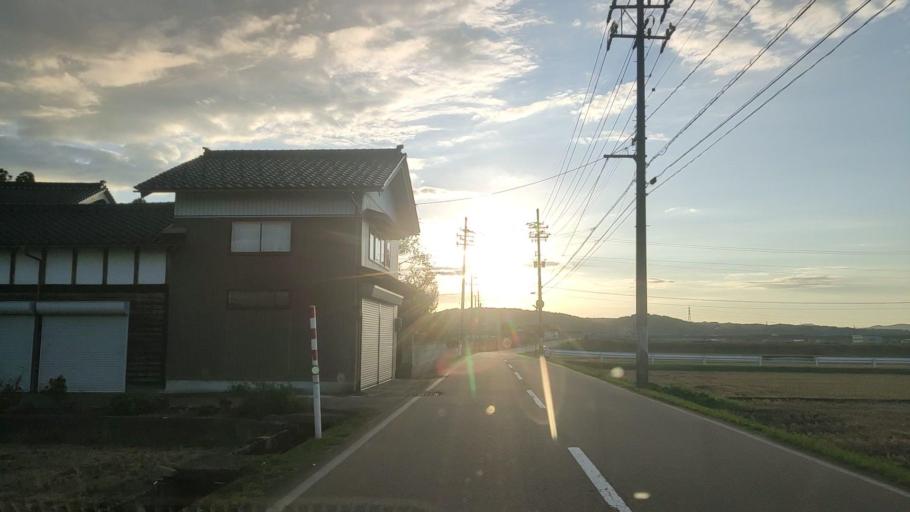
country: JP
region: Toyama
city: Nanto-shi
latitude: 36.6055
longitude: 136.9103
